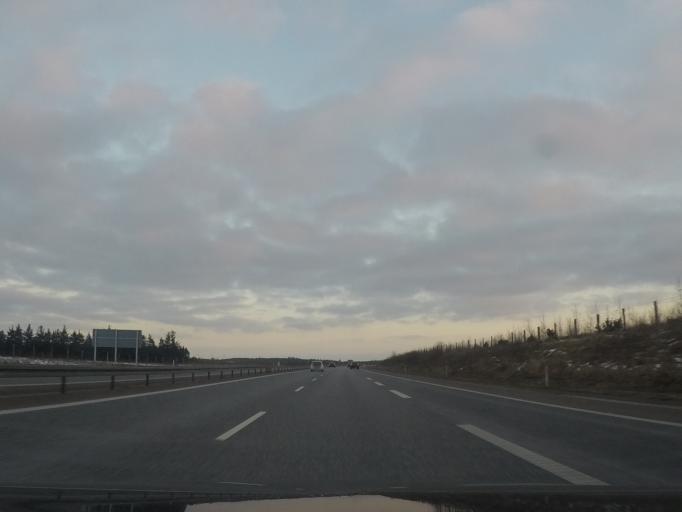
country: DK
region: Central Jutland
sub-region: Herning Kommune
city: Lind
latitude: 56.0135
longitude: 9.0309
